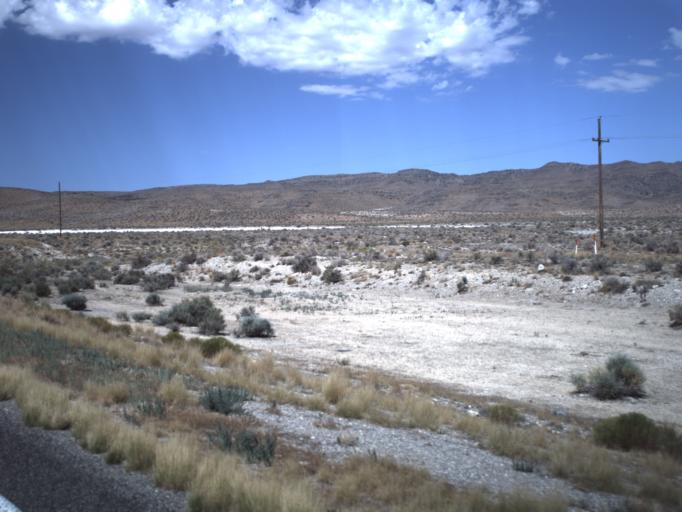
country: US
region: Utah
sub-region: Beaver County
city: Milford
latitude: 39.0625
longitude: -113.2410
